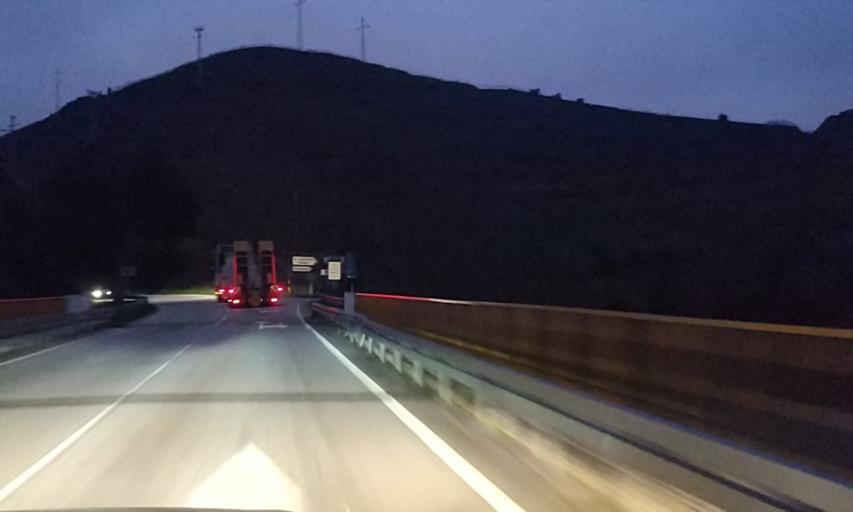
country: PT
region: Viseu
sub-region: Armamar
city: Armamar
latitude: 41.1418
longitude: -7.7004
